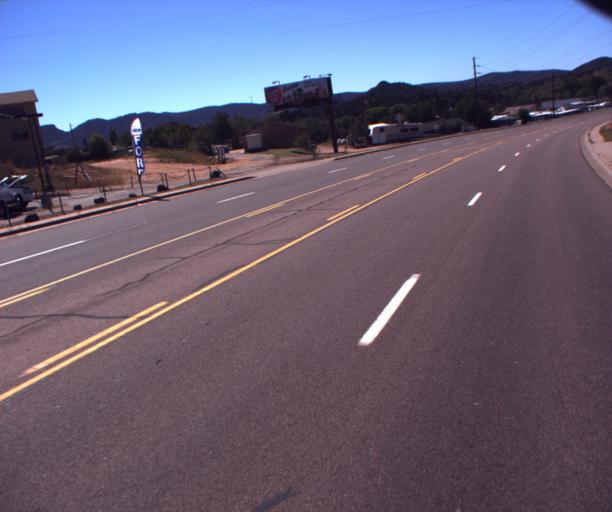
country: US
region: Arizona
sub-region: Gila County
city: Star Valley
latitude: 34.2568
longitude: -111.2547
